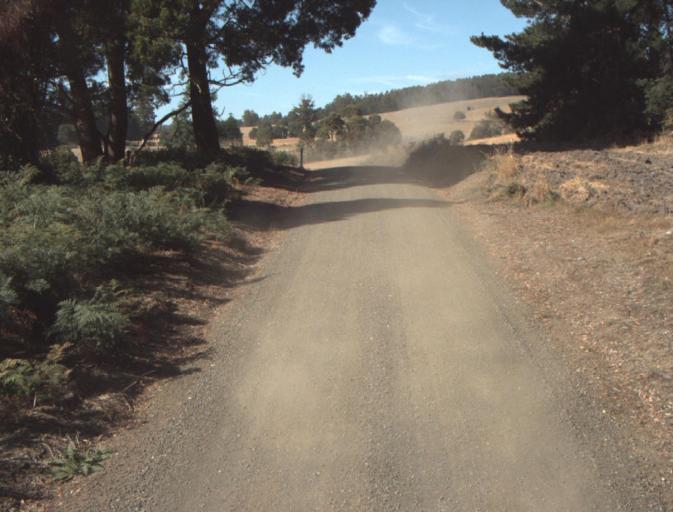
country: AU
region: Tasmania
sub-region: Launceston
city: Mayfield
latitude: -41.1687
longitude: 147.2115
